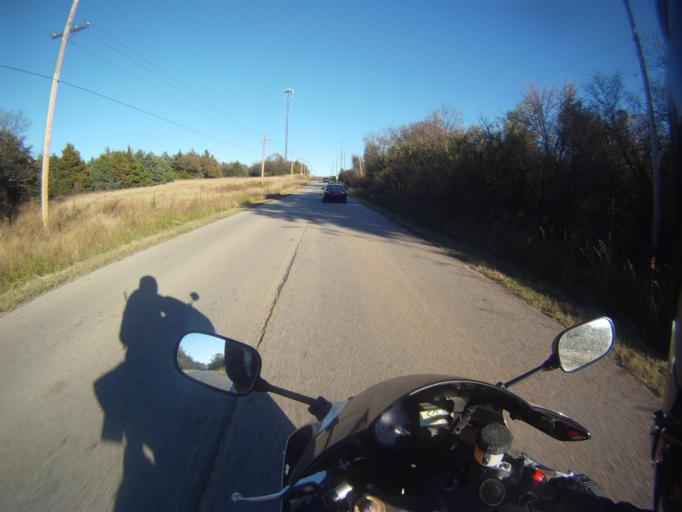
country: US
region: Oklahoma
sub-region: Payne County
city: Stillwater
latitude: 36.1303
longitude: -97.0988
